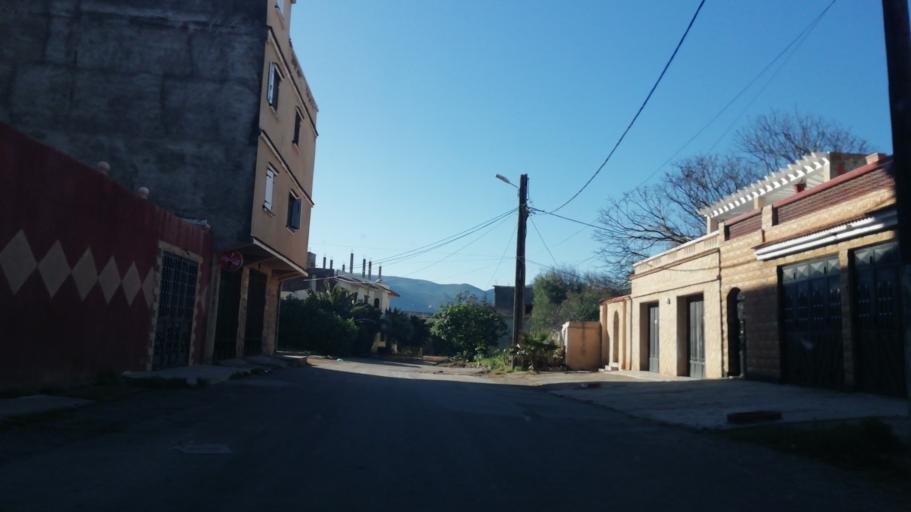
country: DZ
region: Oran
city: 'Ain el Turk
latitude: 35.7216
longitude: -0.8518
